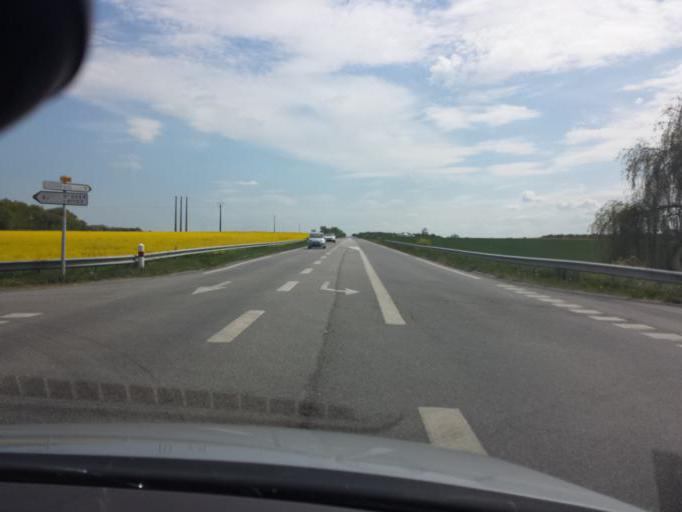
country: FR
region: Haute-Normandie
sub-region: Departement de l'Eure
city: Breteuil
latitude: 48.8010
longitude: 0.9221
